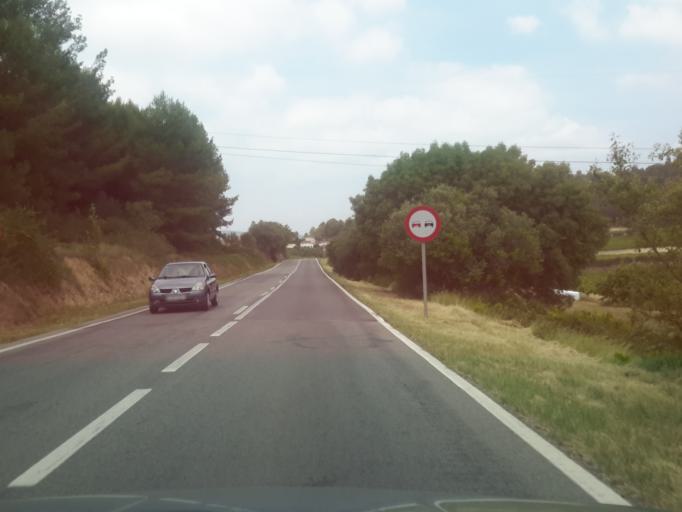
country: ES
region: Catalonia
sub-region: Provincia de Barcelona
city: Vilobi del Penedes
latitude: 41.3776
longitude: 1.6437
